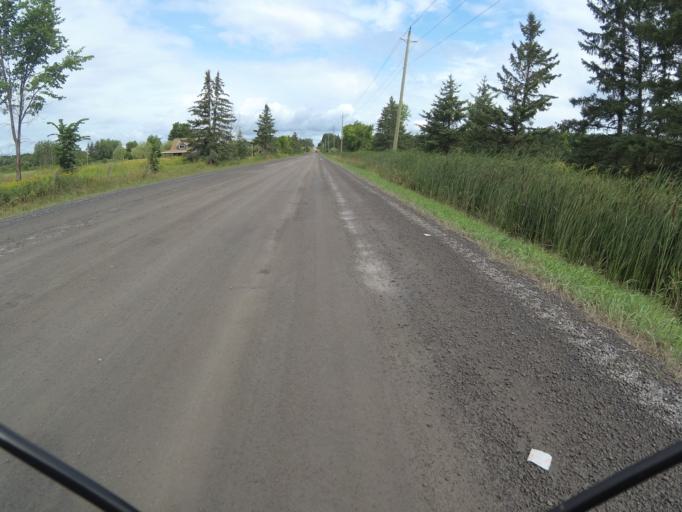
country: CA
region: Ontario
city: Clarence-Rockland
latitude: 45.4815
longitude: -75.3095
